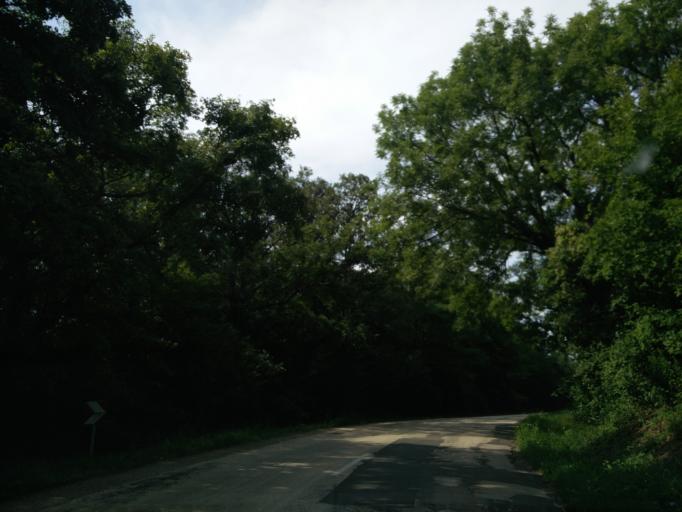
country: HU
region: Fejer
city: Etyek
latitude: 47.4407
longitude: 18.7027
